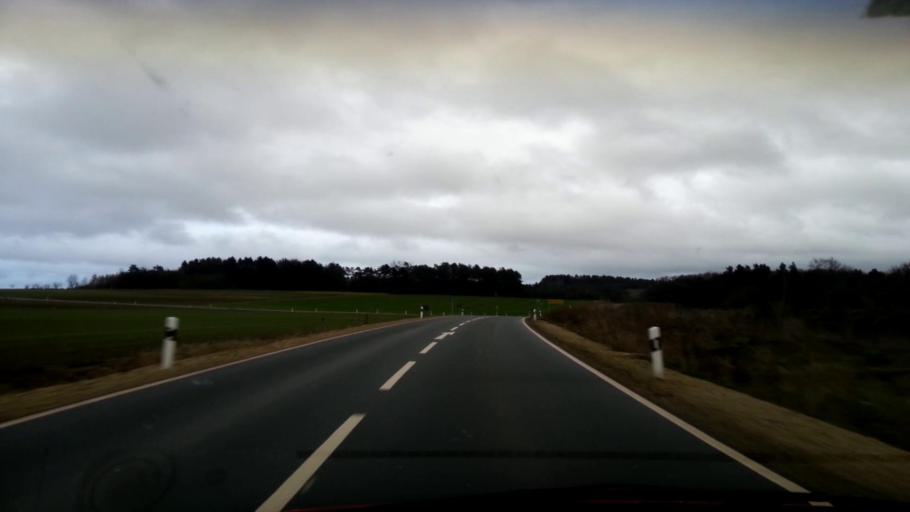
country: DE
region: Bavaria
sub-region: Upper Franconia
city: Poxdorf
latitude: 49.9253
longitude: 11.0872
